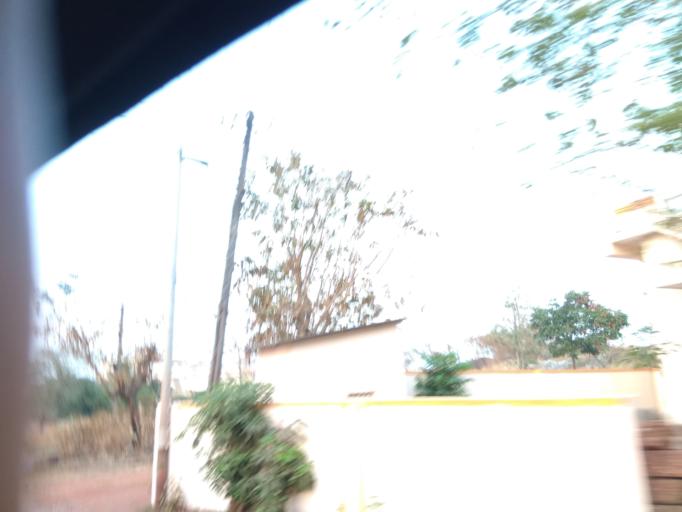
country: IN
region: Karnataka
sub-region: Dakshina Kannada
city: Mangalore
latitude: 12.9270
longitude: 74.8674
